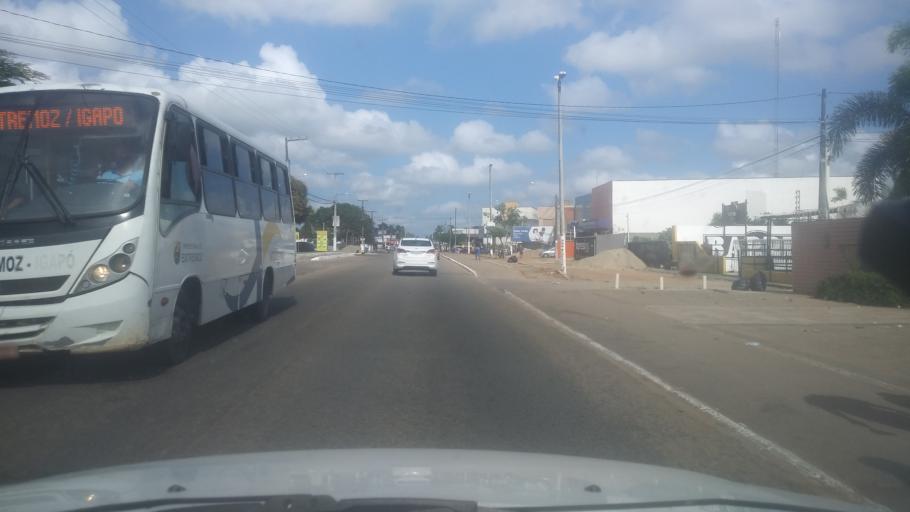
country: BR
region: Rio Grande do Norte
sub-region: Extremoz
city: Extremoz
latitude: -5.7044
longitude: -35.2924
